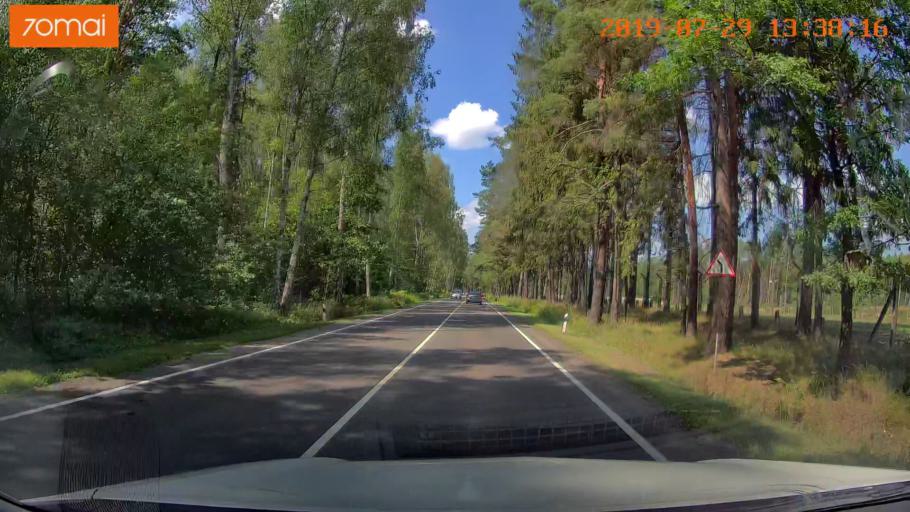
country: RU
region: Kaliningrad
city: Volochayevskoye
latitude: 54.7201
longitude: 20.1732
